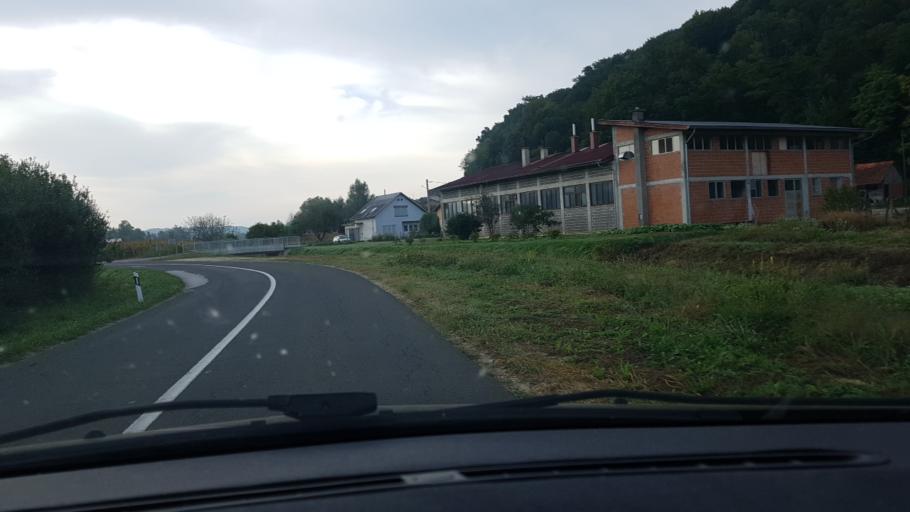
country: HR
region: Krapinsko-Zagorska
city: Zlatar
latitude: 46.1025
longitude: 16.0216
